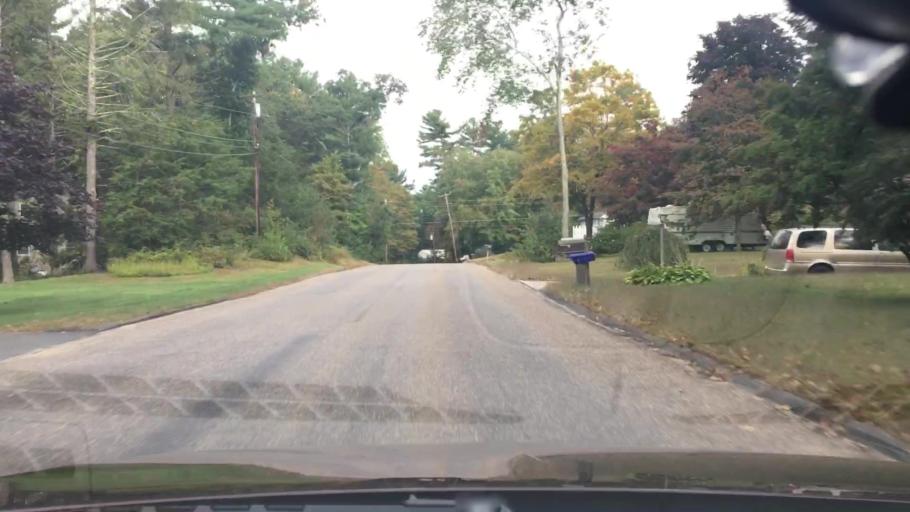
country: US
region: Connecticut
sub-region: Tolland County
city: Stafford
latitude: 41.9930
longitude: -72.3125
